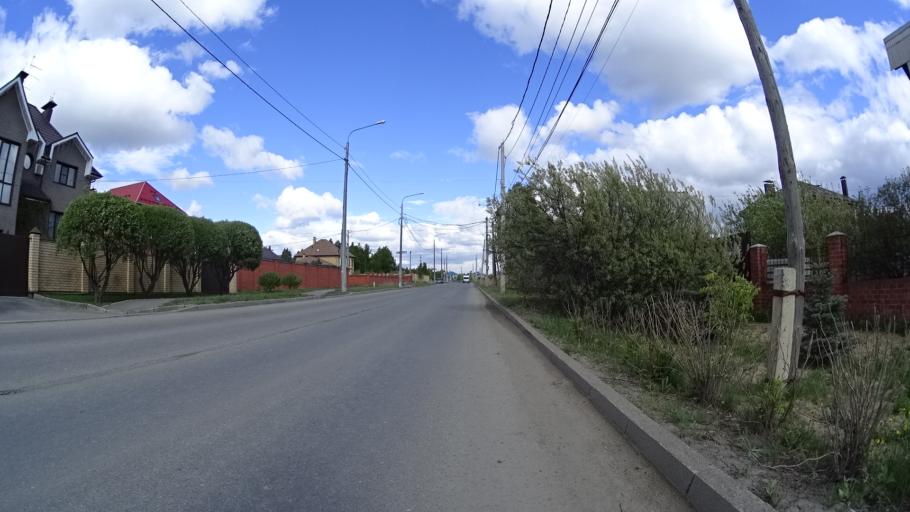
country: RU
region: Chelyabinsk
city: Sargazy
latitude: 55.1522
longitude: 61.2592
